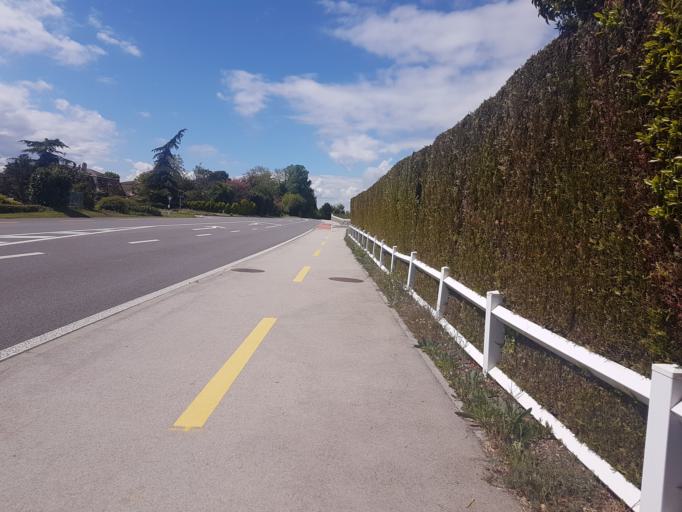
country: CH
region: Vaud
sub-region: Nyon District
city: Gland
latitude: 46.4303
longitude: 6.3013
